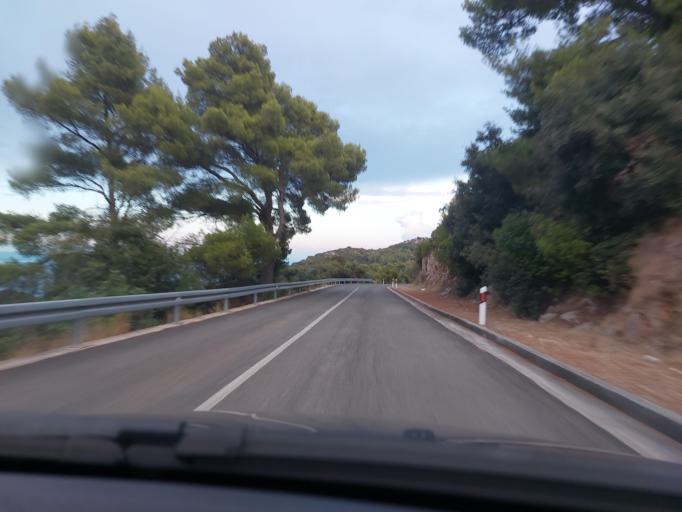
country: HR
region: Dubrovacko-Neretvanska
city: Smokvica
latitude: 42.7685
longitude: 16.8659
